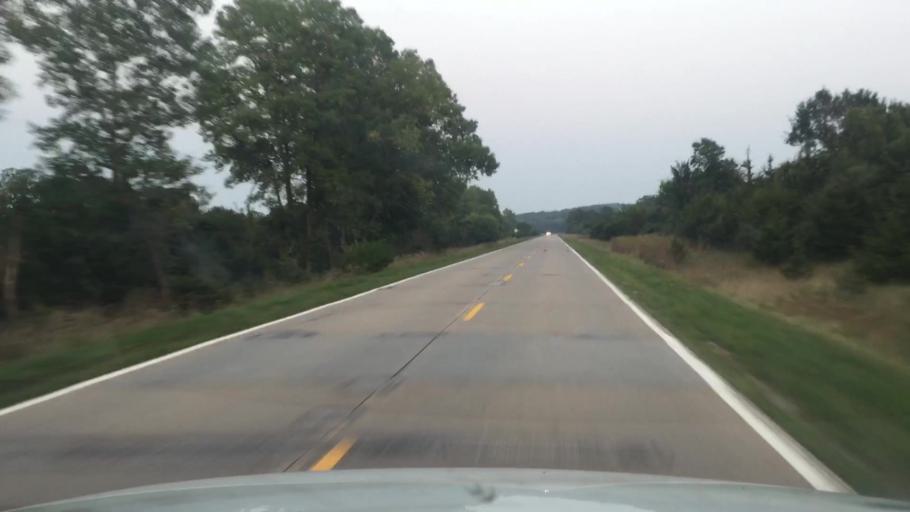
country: US
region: Iowa
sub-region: Warren County
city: Indianola
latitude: 41.1903
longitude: -93.6320
